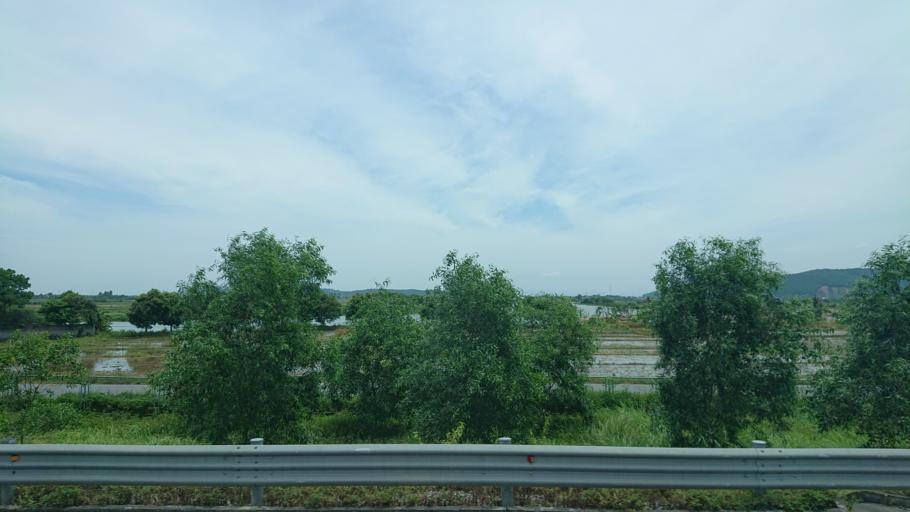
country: VN
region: Hai Phong
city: Tien Lang
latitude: 20.7709
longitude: 106.5967
